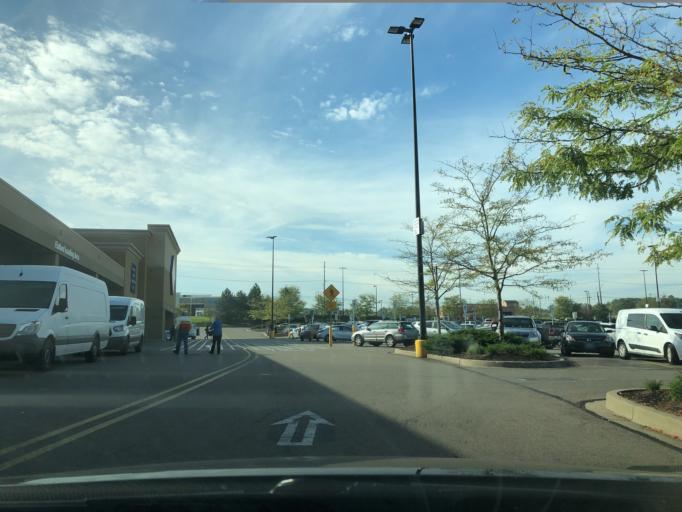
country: US
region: Ohio
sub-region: Hamilton County
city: Glendale
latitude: 39.2890
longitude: -84.4573
